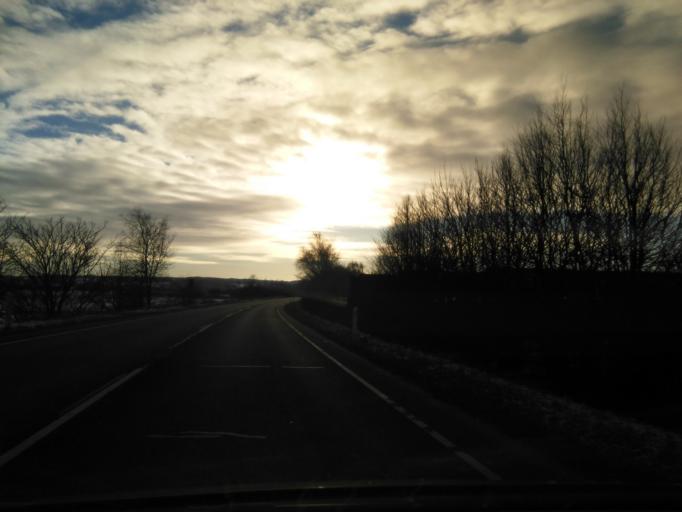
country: DK
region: Central Jutland
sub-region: Arhus Kommune
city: Framlev
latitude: 56.1483
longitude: 10.0070
